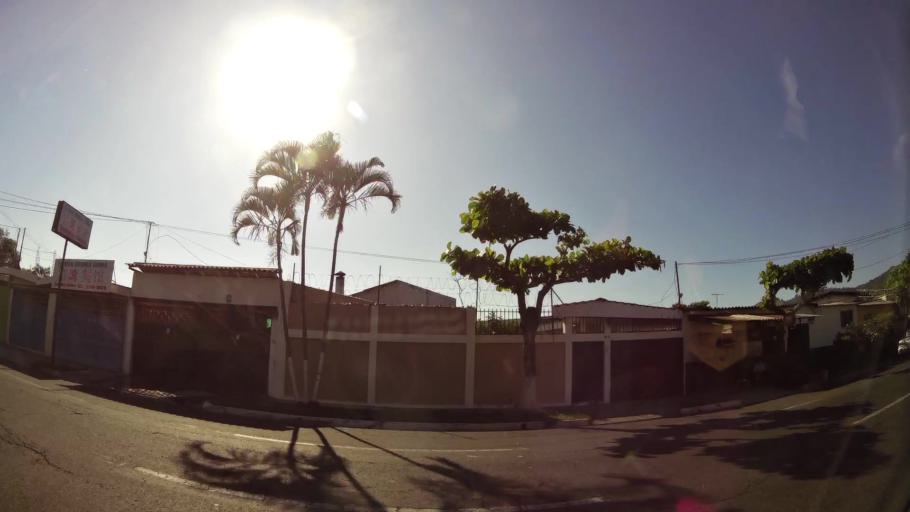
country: SV
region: La Libertad
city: Santa Tecla
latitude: 13.6798
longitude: -89.2943
